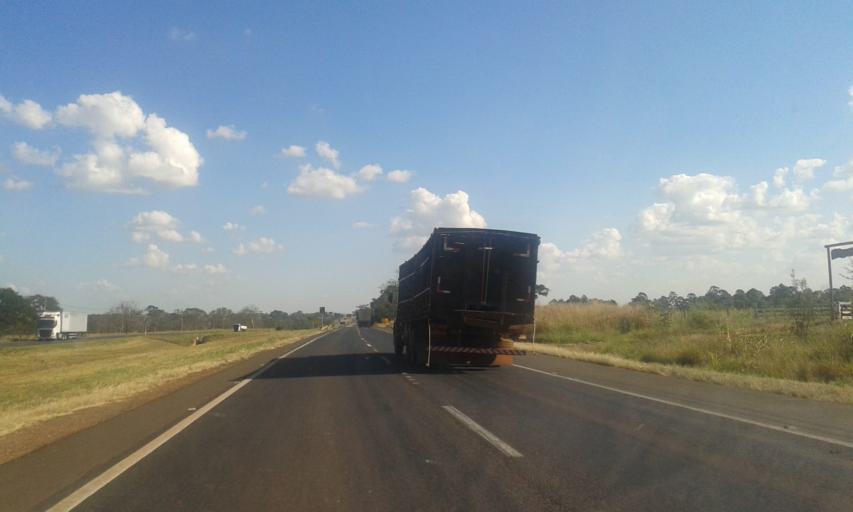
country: BR
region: Minas Gerais
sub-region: Monte Alegre De Minas
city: Monte Alegre de Minas
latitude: -18.8706
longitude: -48.5975
